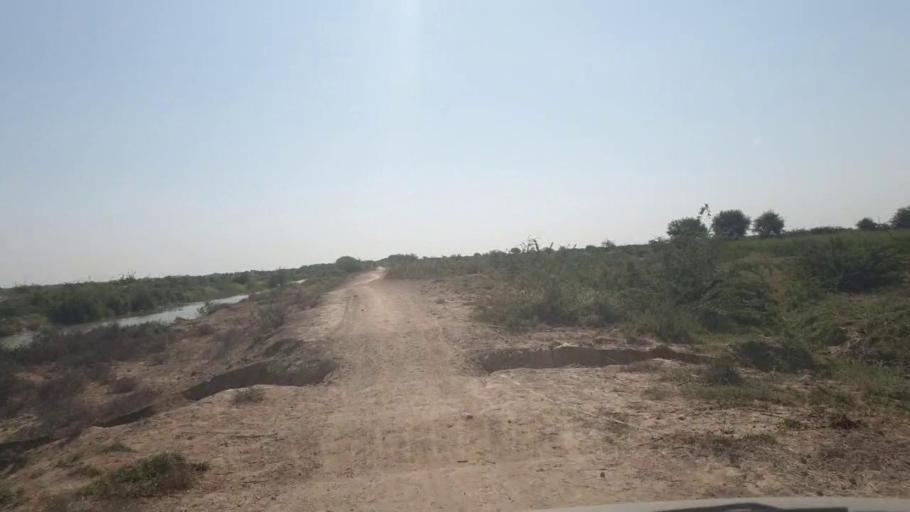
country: PK
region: Sindh
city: Tando Bago
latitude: 24.9137
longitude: 69.1645
